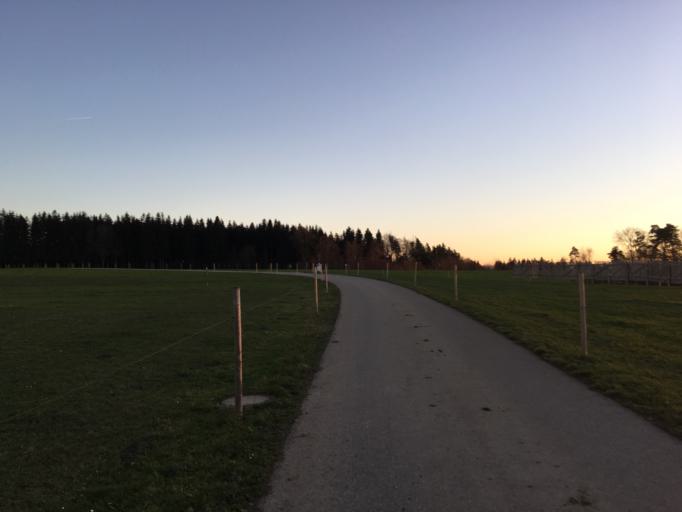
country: DE
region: Bavaria
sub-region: Swabia
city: Wolfertschwenden
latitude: 47.8745
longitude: 10.2768
